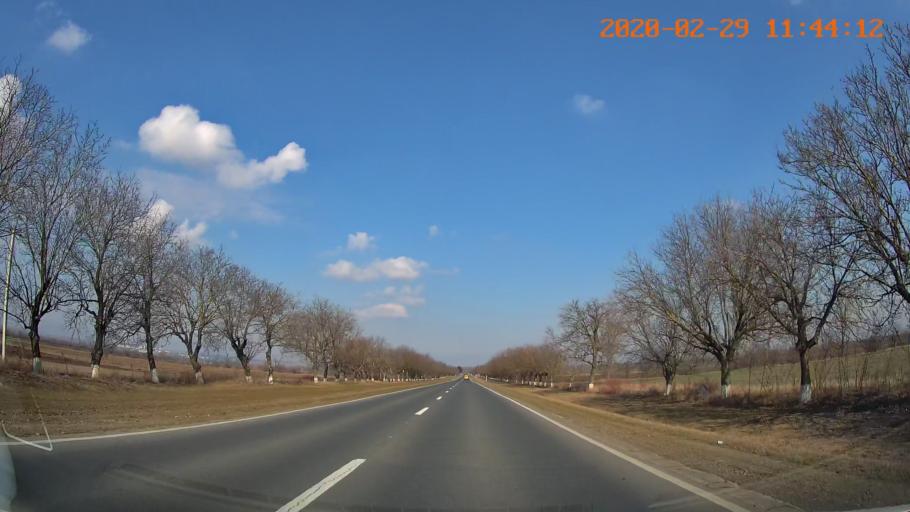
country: MD
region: Rezina
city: Saharna
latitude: 47.7078
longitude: 29.0010
